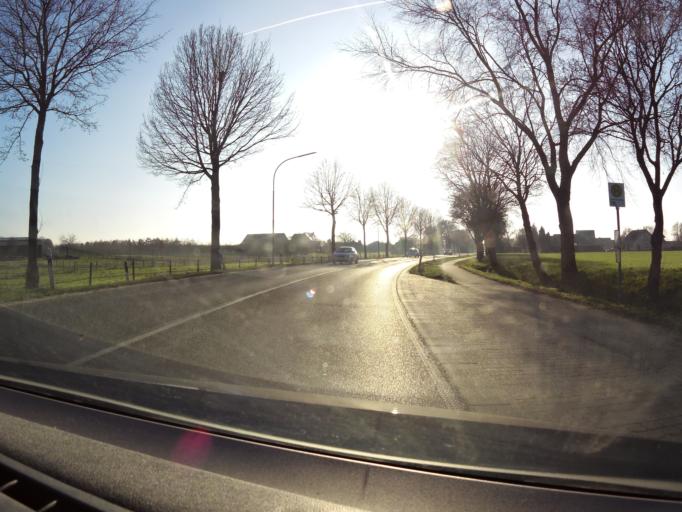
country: DE
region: North Rhine-Westphalia
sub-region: Regierungsbezirk Dusseldorf
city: Bruggen
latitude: 51.2992
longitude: 6.2004
